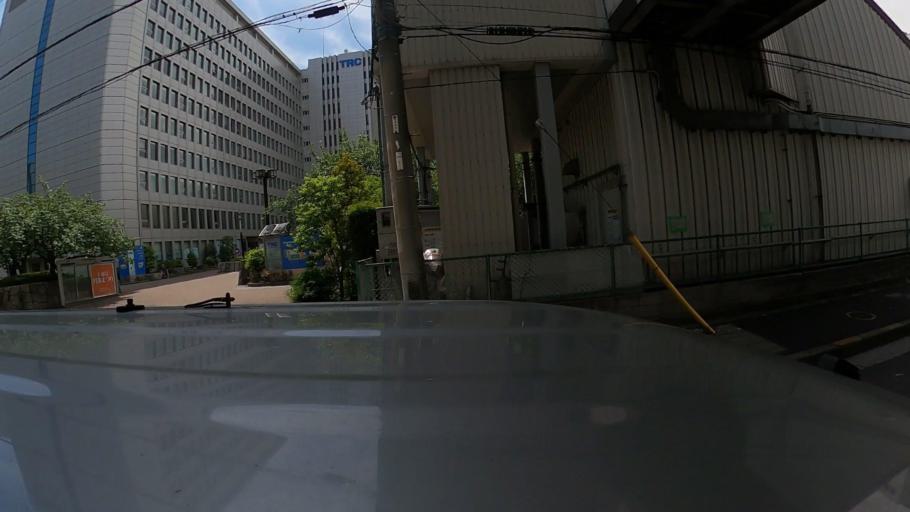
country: JP
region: Kanagawa
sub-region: Kawasaki-shi
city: Kawasaki
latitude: 35.5819
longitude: 139.7490
